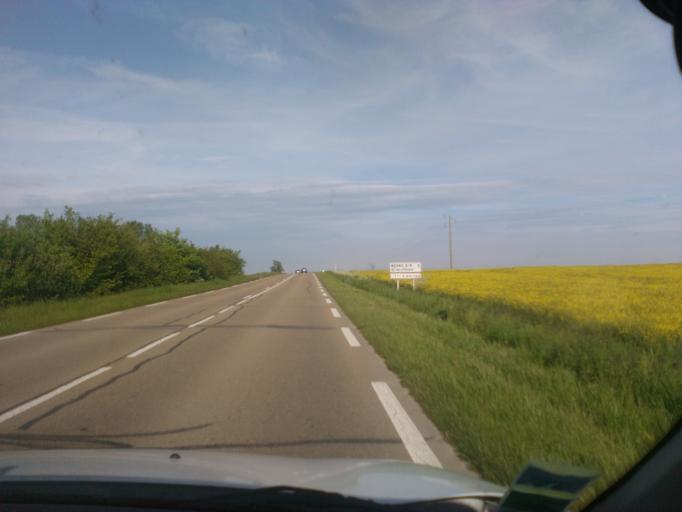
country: FR
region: Champagne-Ardenne
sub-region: Departement de l'Aube
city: Lusigny-sur-Barse
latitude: 48.2425
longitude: 4.3562
